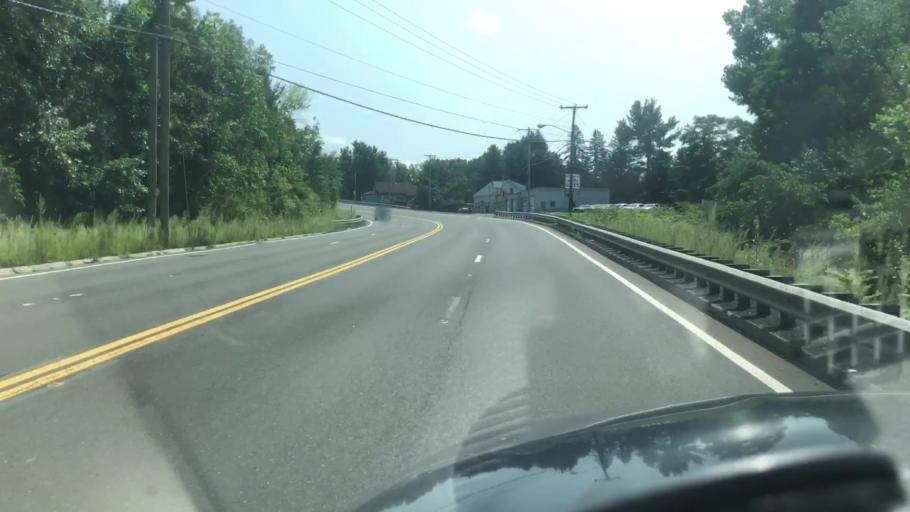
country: US
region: Massachusetts
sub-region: Hampden County
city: West Springfield
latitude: 42.1064
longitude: -72.6821
